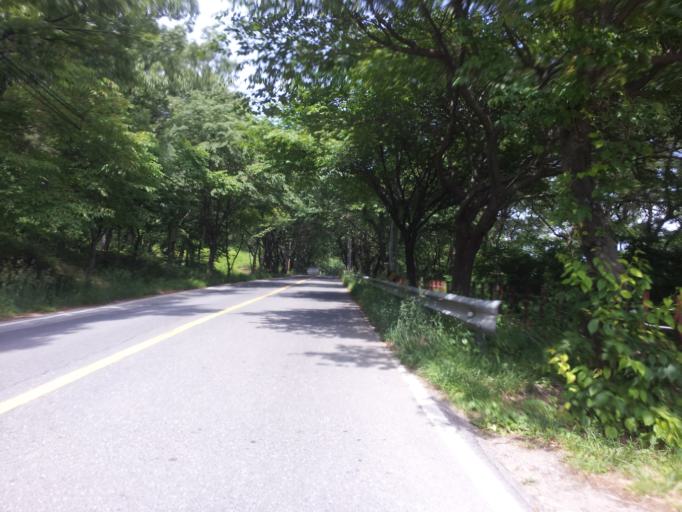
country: KR
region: Daejeon
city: Sintansin
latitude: 36.4328
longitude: 127.4686
